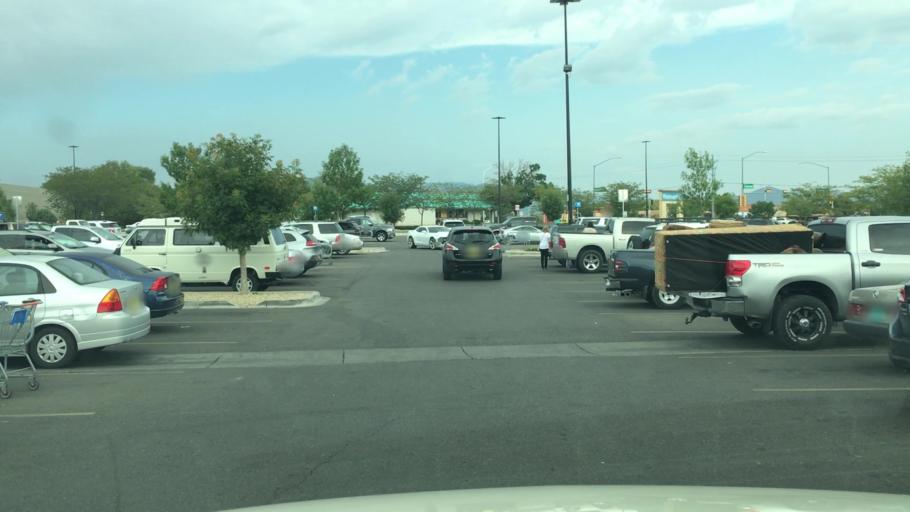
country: US
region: New Mexico
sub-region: Santa Fe County
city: Agua Fria
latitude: 35.6525
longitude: -105.9990
